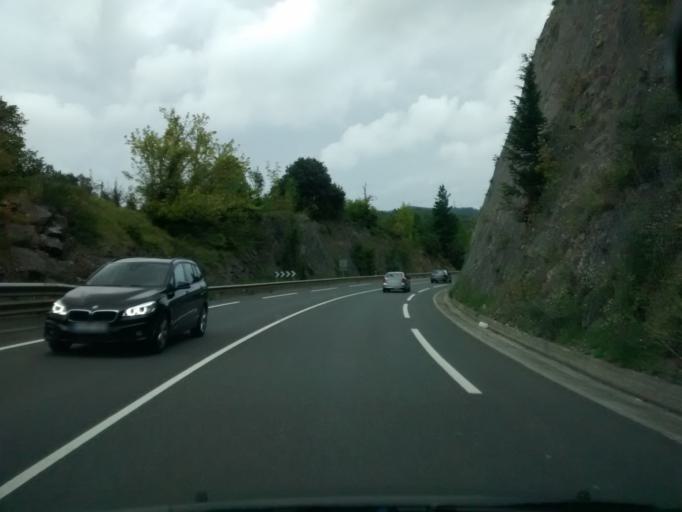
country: ES
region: Basque Country
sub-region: Provincia de Guipuzcoa
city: Arrasate / Mondragon
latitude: 43.0616
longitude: -2.4910
